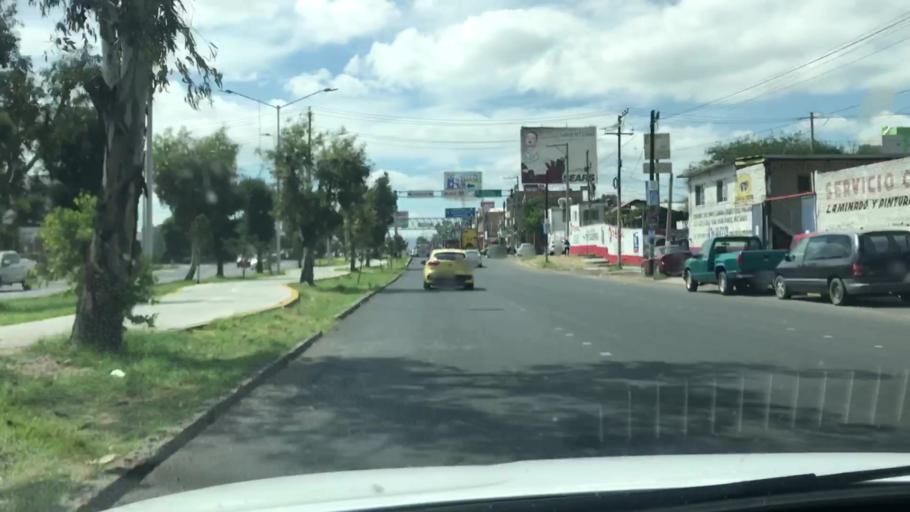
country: MX
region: Guanajuato
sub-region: Celaya
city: Roque
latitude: 20.5556
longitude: -100.8226
